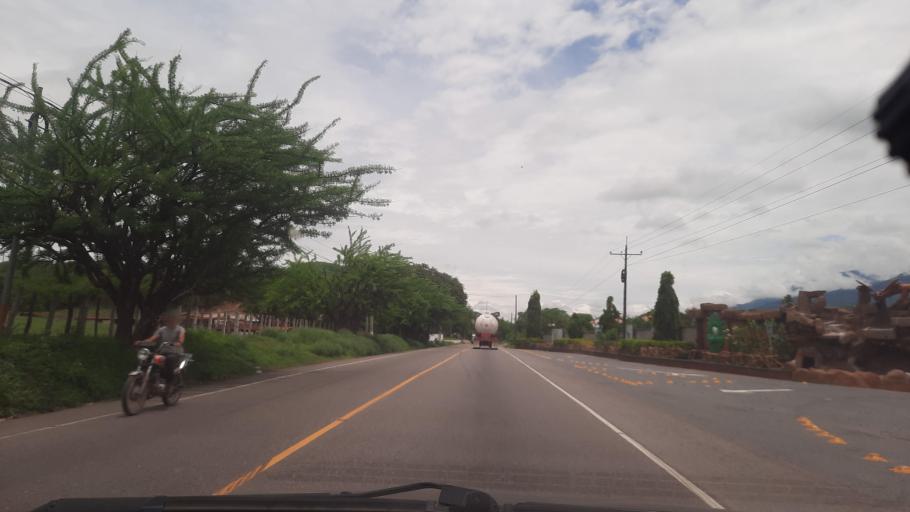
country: GT
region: Zacapa
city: Rio Hondo
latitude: 15.0822
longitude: -89.4832
